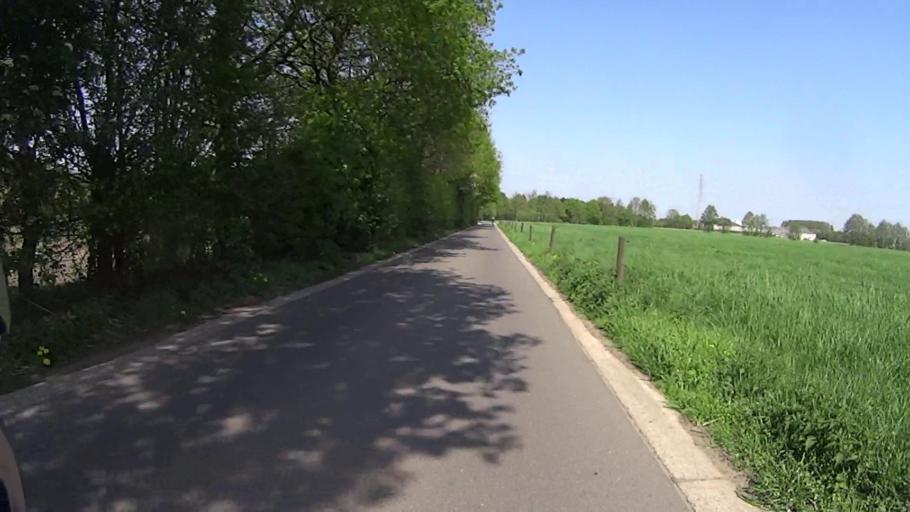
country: BE
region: Flanders
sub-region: Provincie Antwerpen
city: Sint-Amands
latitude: 51.0672
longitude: 4.2153
